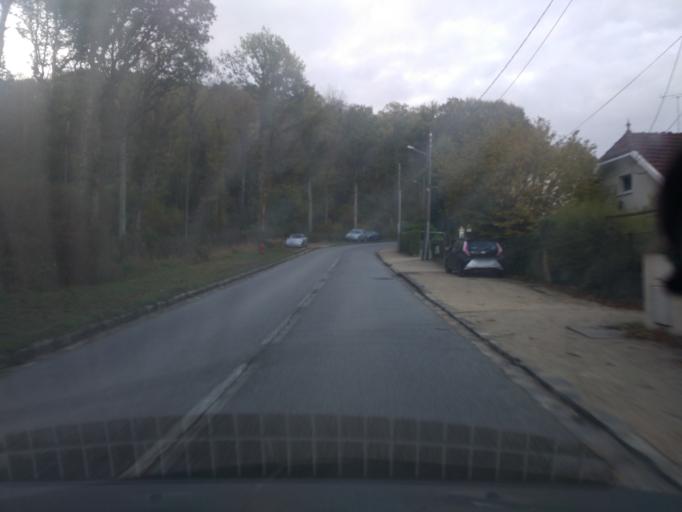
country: FR
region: Ile-de-France
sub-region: Departement des Yvelines
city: Saint-Remy-les-Chevreuse
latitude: 48.6963
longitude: 2.0669
